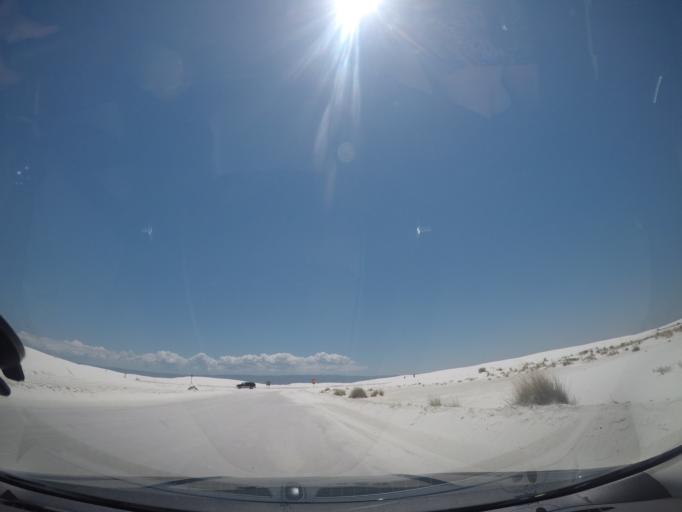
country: US
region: New Mexico
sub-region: Otero County
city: Holloman Air Force Base
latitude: 32.8103
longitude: -106.2629
